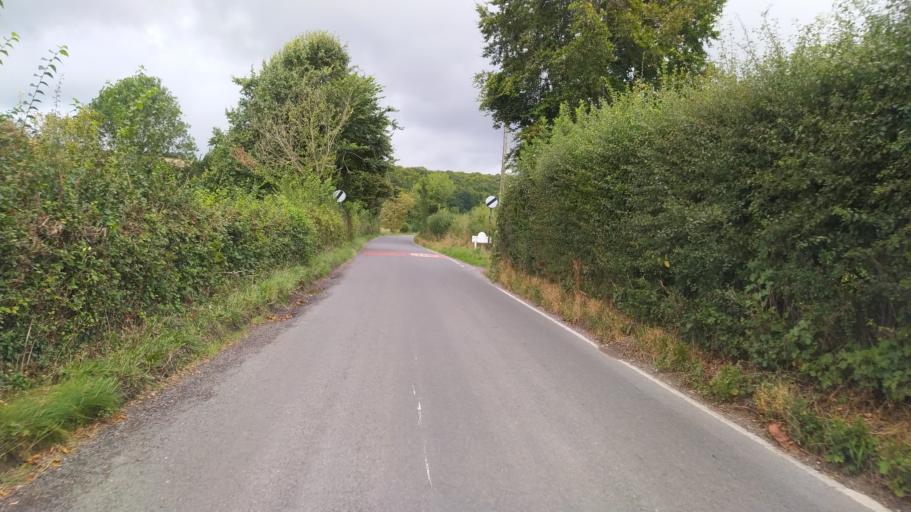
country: GB
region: England
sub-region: Hampshire
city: Petersfield
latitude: 50.9961
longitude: -1.0361
